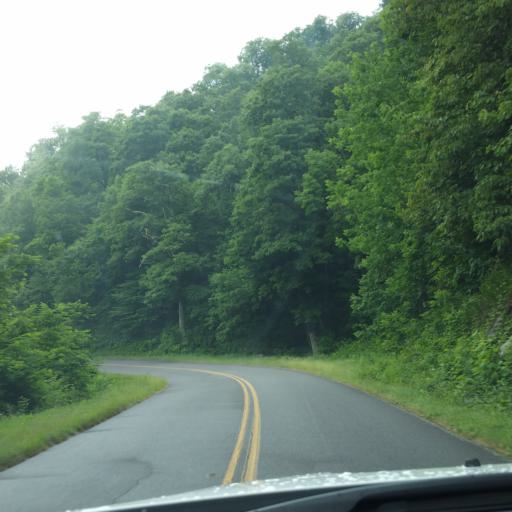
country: US
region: North Carolina
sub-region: Transylvania County
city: Brevard
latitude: 35.3554
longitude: -82.7996
